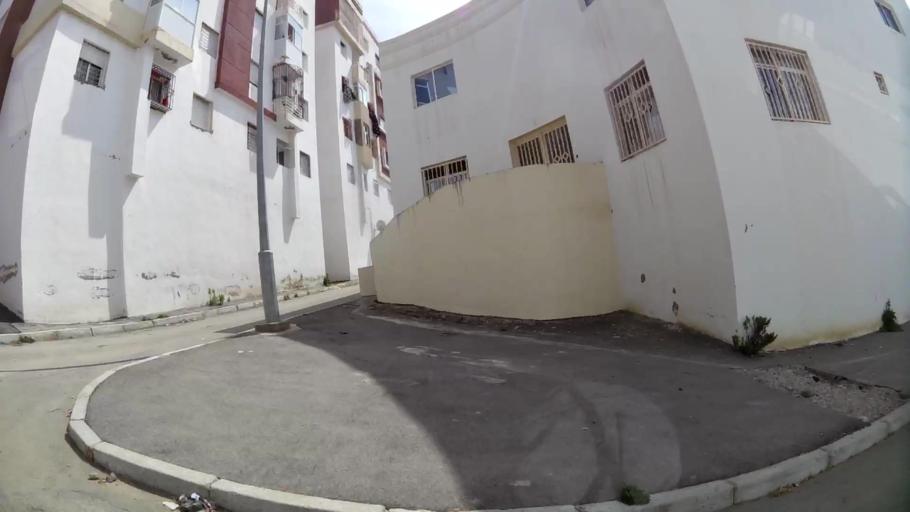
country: MA
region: Tanger-Tetouan
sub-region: Tanger-Assilah
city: Tangier
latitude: 35.7610
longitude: -5.7609
